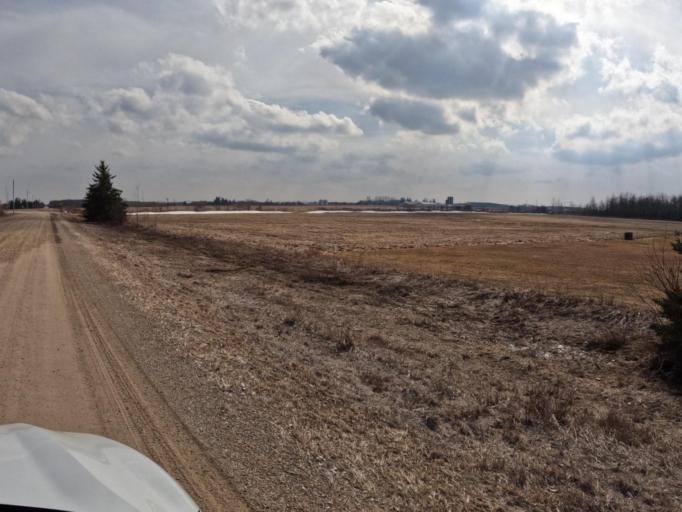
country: CA
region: Ontario
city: Shelburne
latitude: 43.9336
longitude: -80.3091
